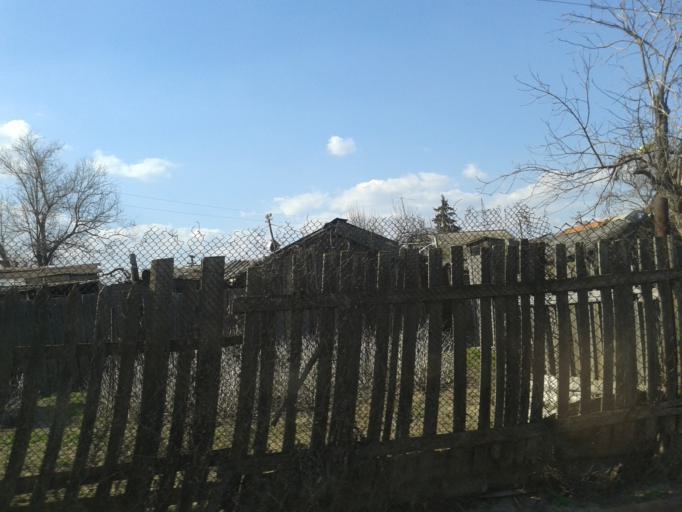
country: RU
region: Volgograd
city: Volgograd
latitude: 48.6266
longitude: 44.3795
